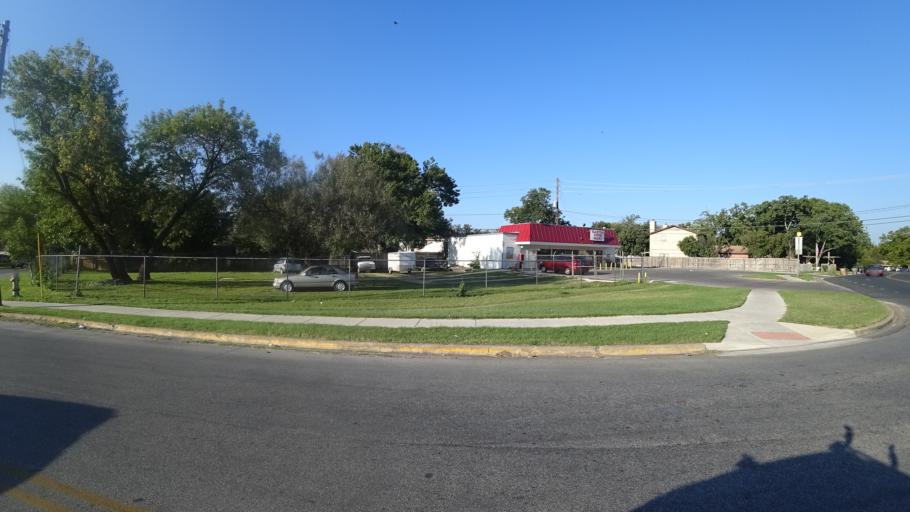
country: US
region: Texas
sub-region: Travis County
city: Austin
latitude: 30.3118
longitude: -97.6854
